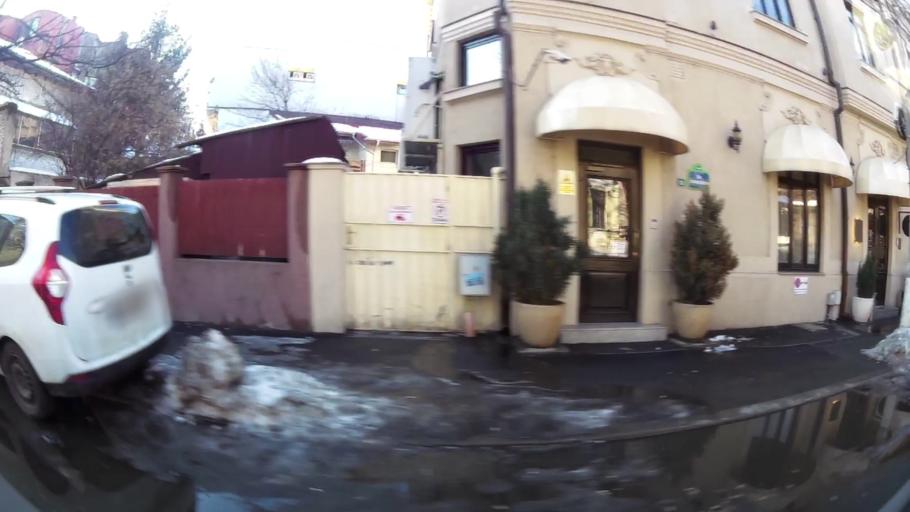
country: RO
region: Bucuresti
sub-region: Municipiul Bucuresti
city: Bucharest
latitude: 44.4361
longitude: 26.1167
